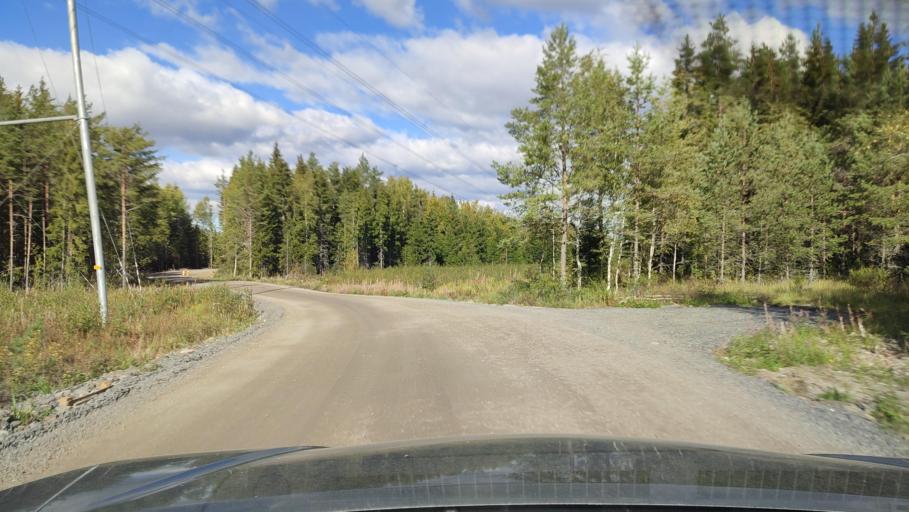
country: FI
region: Southern Ostrobothnia
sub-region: Suupohja
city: Karijoki
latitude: 62.1839
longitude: 21.5901
